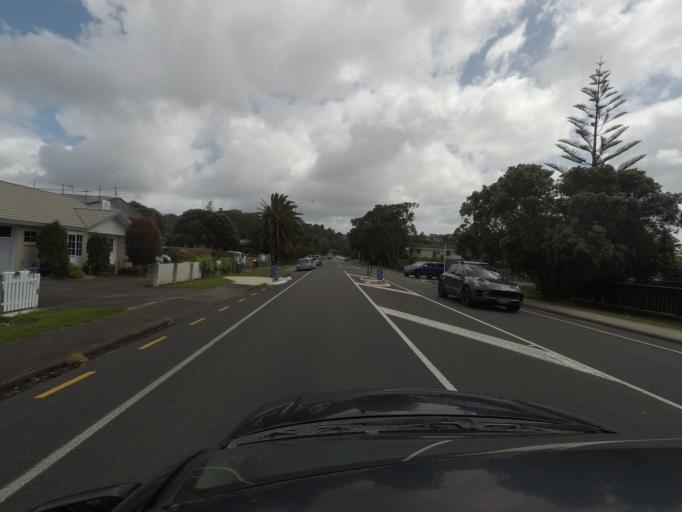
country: NZ
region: Auckland
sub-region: Auckland
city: Rothesay Bay
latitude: -36.5788
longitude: 174.6921
